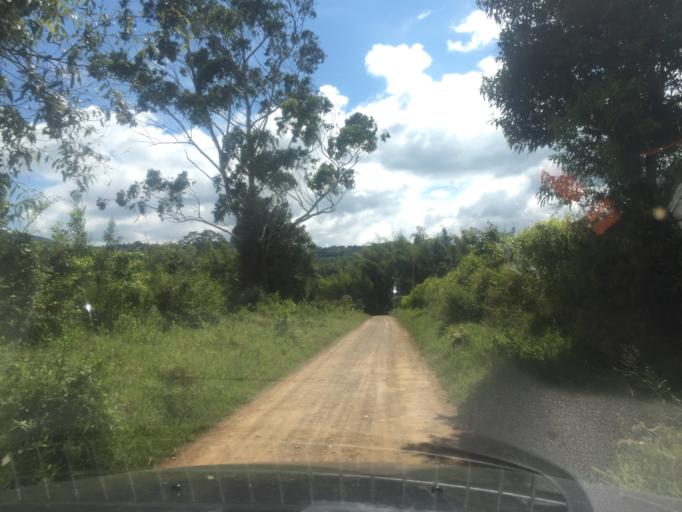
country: CO
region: Valle del Cauca
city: Yumbo
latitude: 3.6659
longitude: -76.5603
